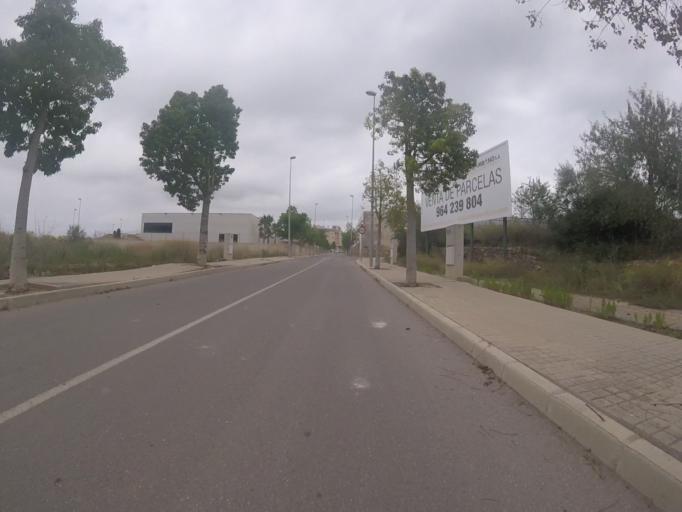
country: ES
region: Valencia
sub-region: Provincia de Castello
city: Cabanes
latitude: 40.1522
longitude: 0.0472
